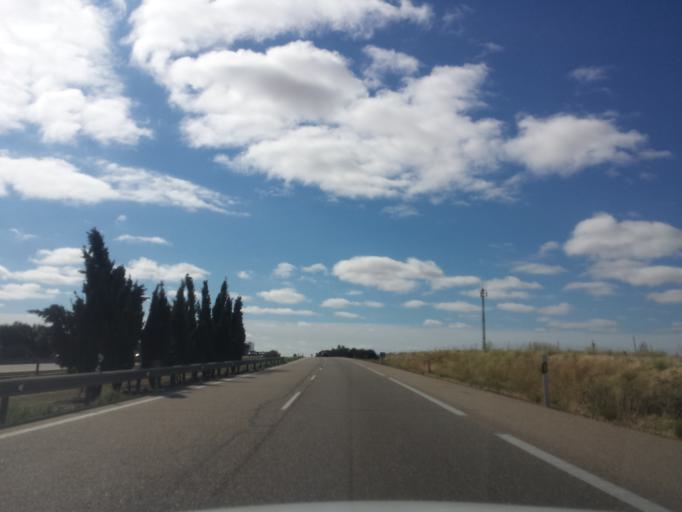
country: ES
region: Castille and Leon
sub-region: Provincia de Zamora
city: Cerecinos de Campos
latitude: 41.8937
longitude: -5.4709
